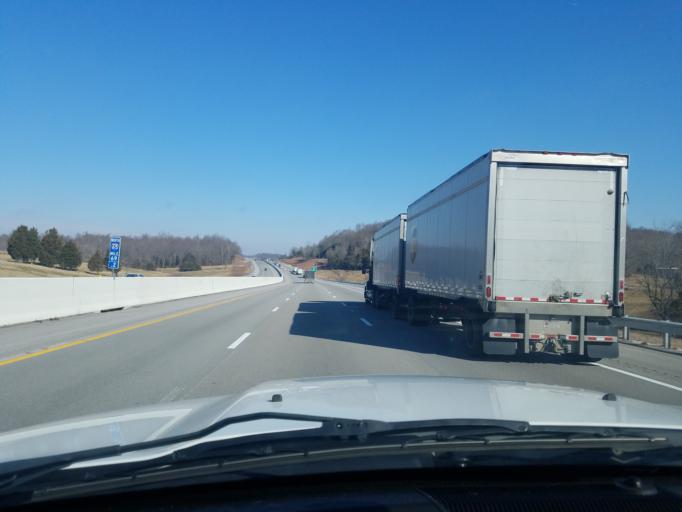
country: US
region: Kentucky
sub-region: Hart County
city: Munfordville
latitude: 37.3624
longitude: -85.8946
